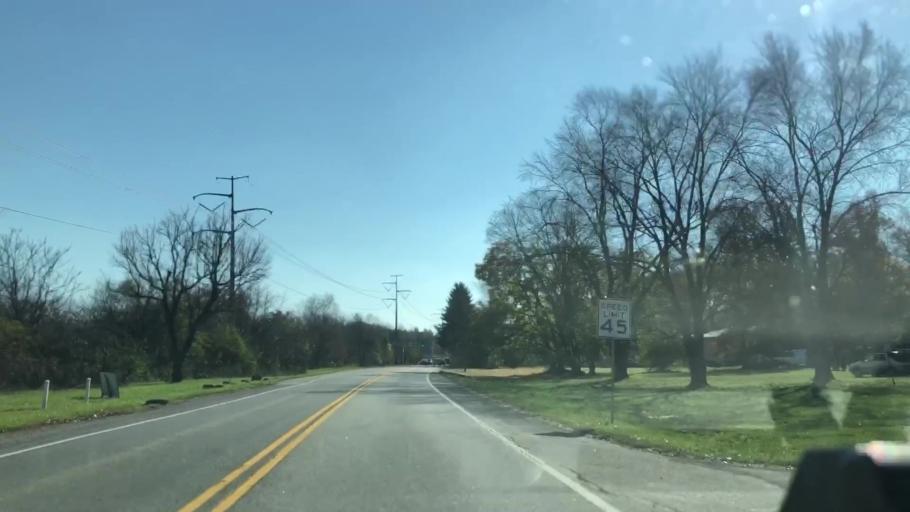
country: US
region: Pennsylvania
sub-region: Montgomery County
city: Sanatoga
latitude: 40.2017
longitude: -75.5855
